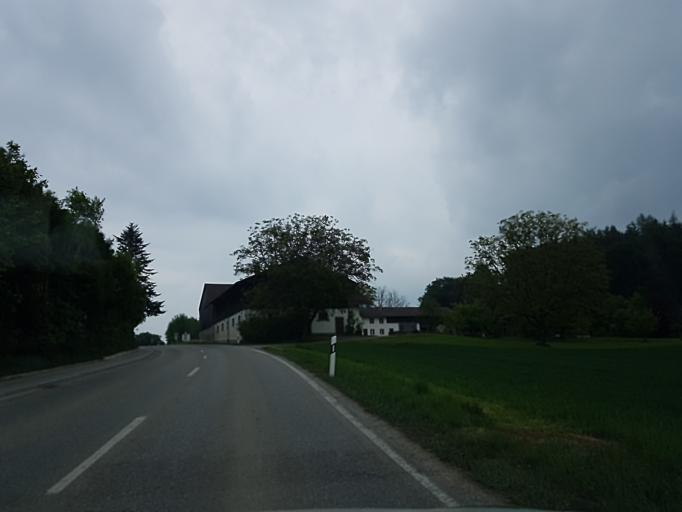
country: DE
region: Bavaria
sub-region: Upper Bavaria
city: Ebersberg
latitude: 48.0899
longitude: 11.9721
